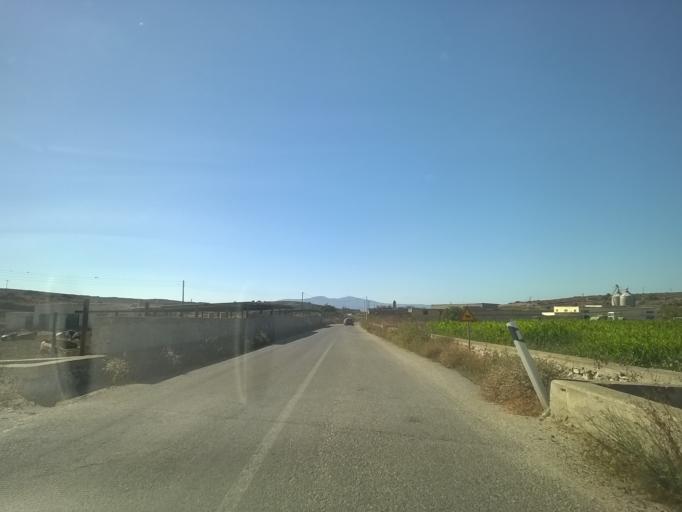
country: GR
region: South Aegean
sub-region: Nomos Kykladon
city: Naxos
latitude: 37.0425
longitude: 25.4210
